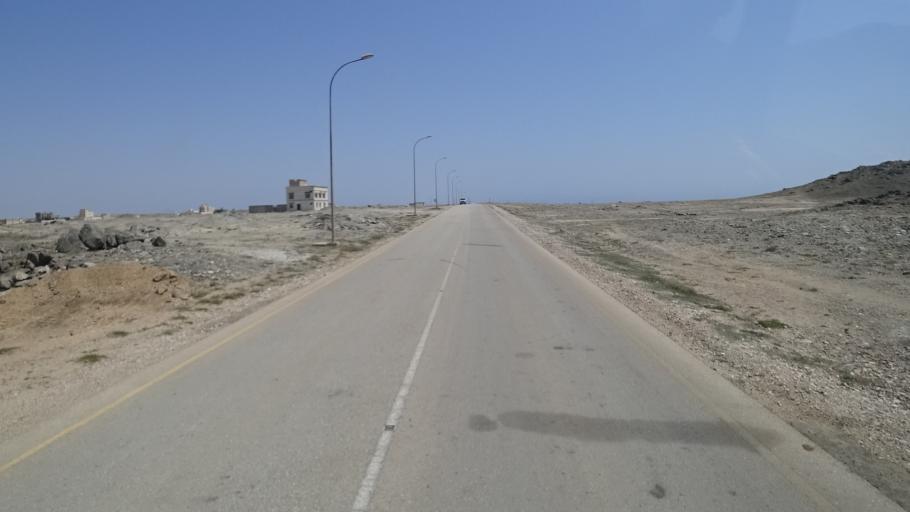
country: OM
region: Zufar
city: Salalah
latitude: 16.9700
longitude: 54.7260
